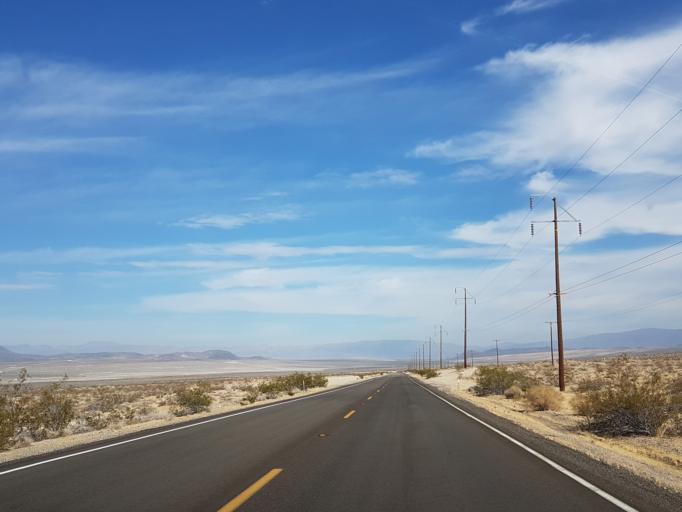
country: US
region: California
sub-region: Kern County
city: Ridgecrest
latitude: 35.6401
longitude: -117.5585
